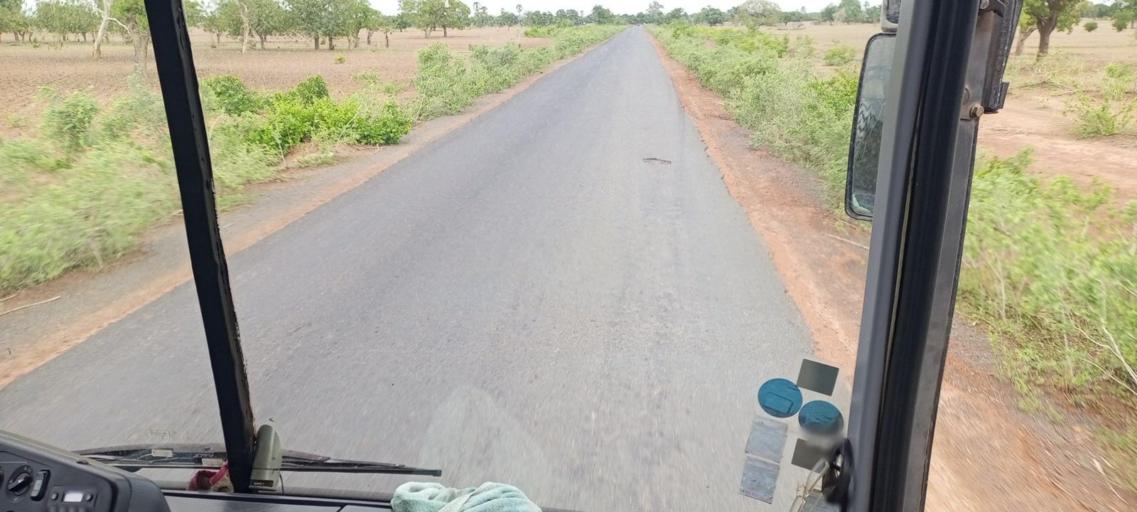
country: ML
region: Segou
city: Bla
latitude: 12.7443
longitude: -5.7303
